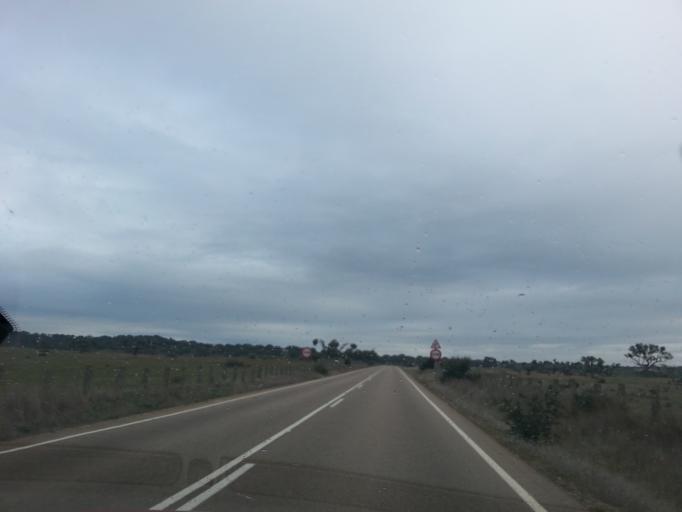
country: ES
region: Castille and Leon
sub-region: Provincia de Salamanca
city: Berrocal de Huebra
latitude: 40.7032
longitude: -6.0251
